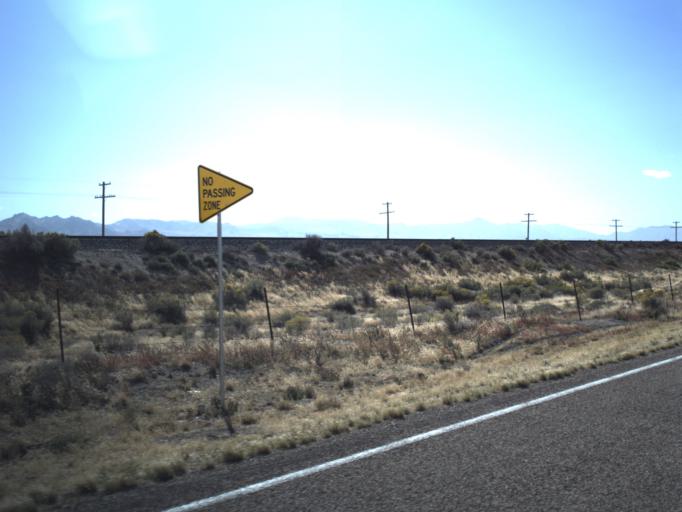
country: US
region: Utah
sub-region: Beaver County
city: Milford
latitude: 38.6685
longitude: -112.9808
